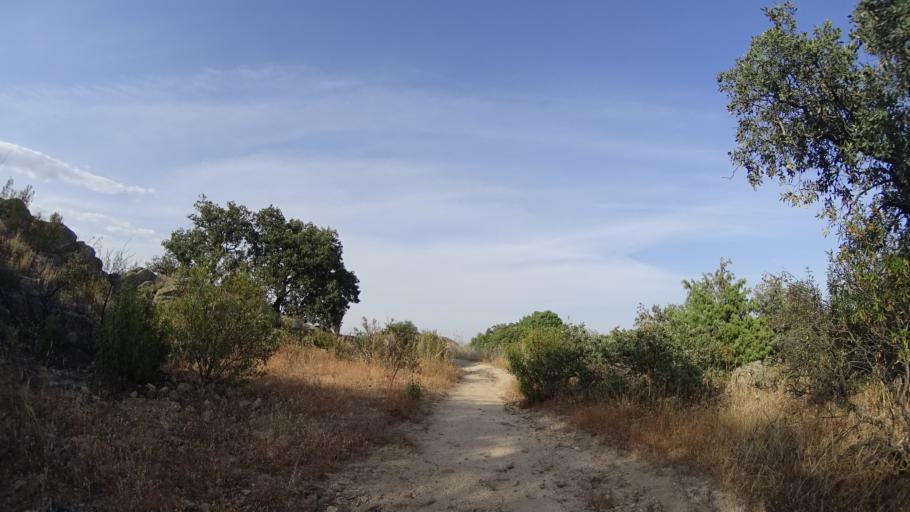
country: ES
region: Madrid
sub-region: Provincia de Madrid
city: Torrelodones
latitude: 40.5908
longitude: -3.9416
